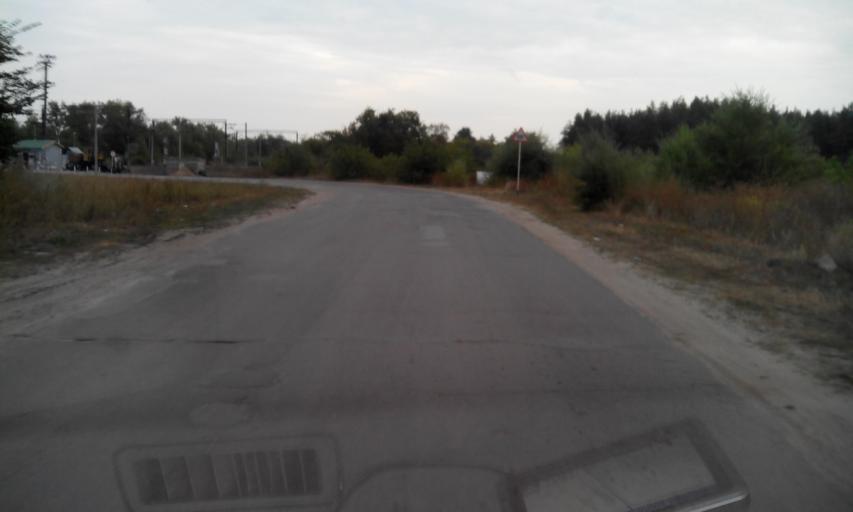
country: RU
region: Samara
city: Balasheyka
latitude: 53.1693
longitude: 48.1386
